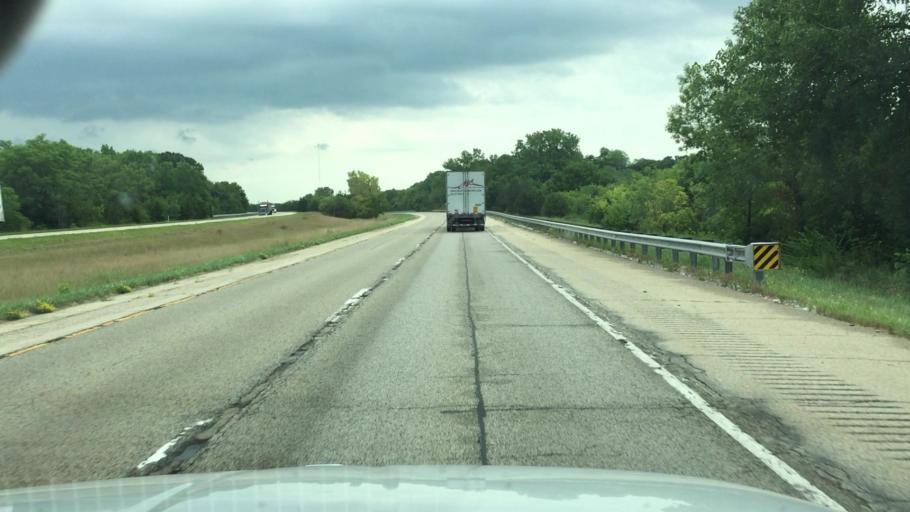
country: US
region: Illinois
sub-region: Peoria County
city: Hanna City
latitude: 40.7941
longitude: -89.8024
